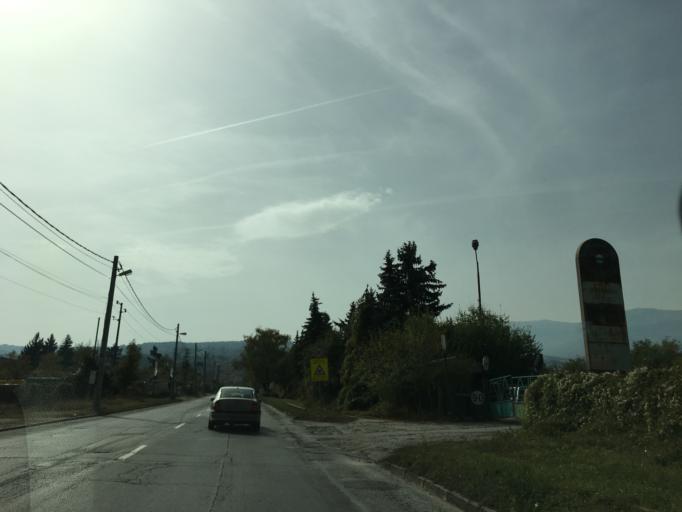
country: BG
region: Sofia-Capital
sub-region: Stolichna Obshtina
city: Sofia
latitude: 42.6176
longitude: 23.4022
